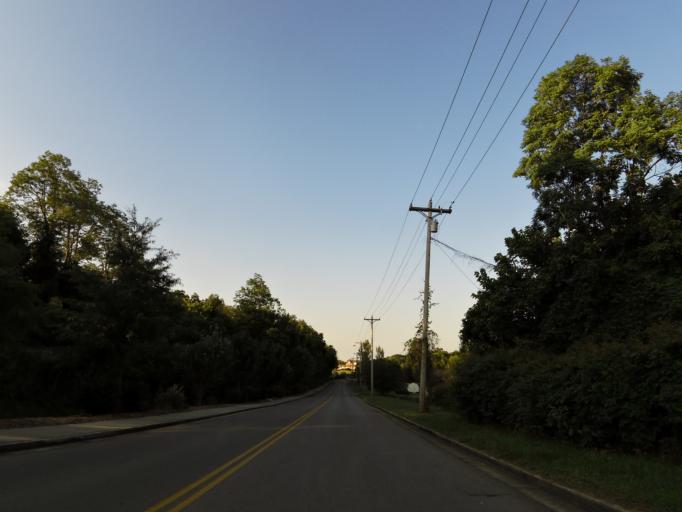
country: US
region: Tennessee
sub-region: McMinn County
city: Athens
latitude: 35.4449
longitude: -84.6005
